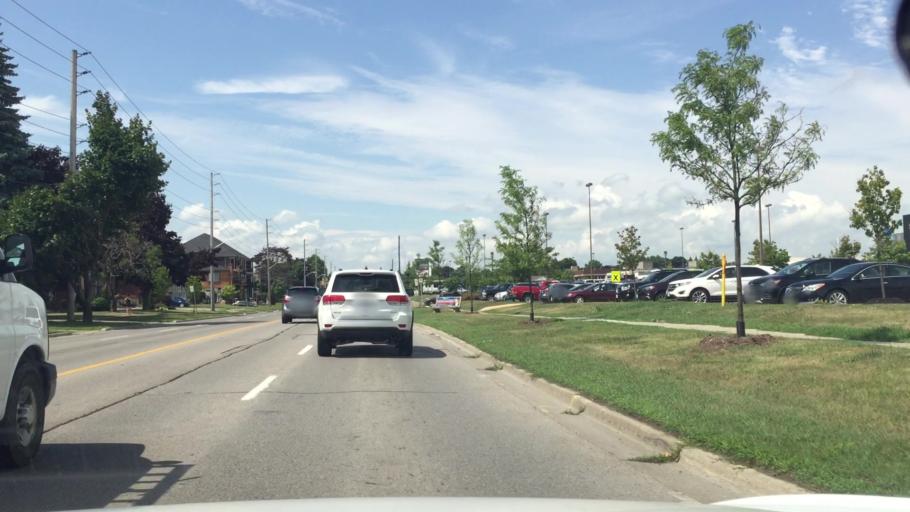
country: CA
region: Ontario
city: Oshawa
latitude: 43.8877
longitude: -78.8808
